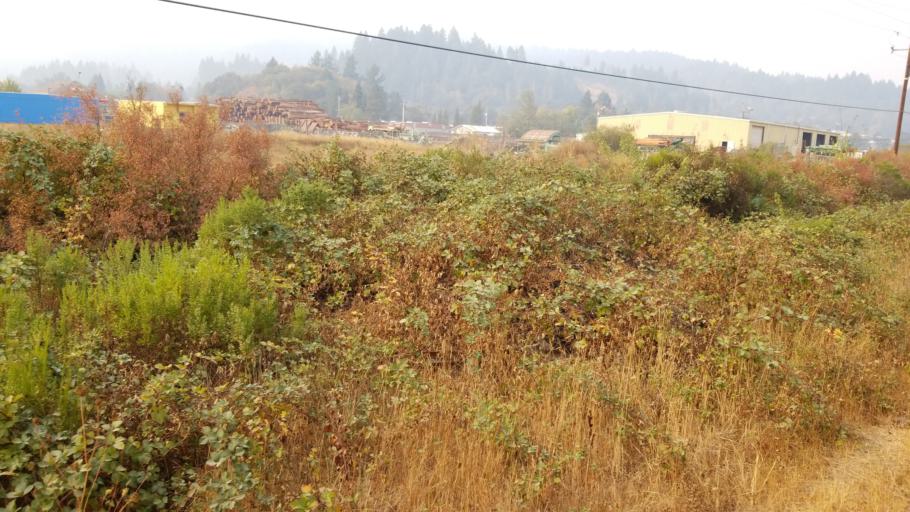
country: US
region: California
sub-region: Mendocino County
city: Willits
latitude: 39.4020
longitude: -123.3575
